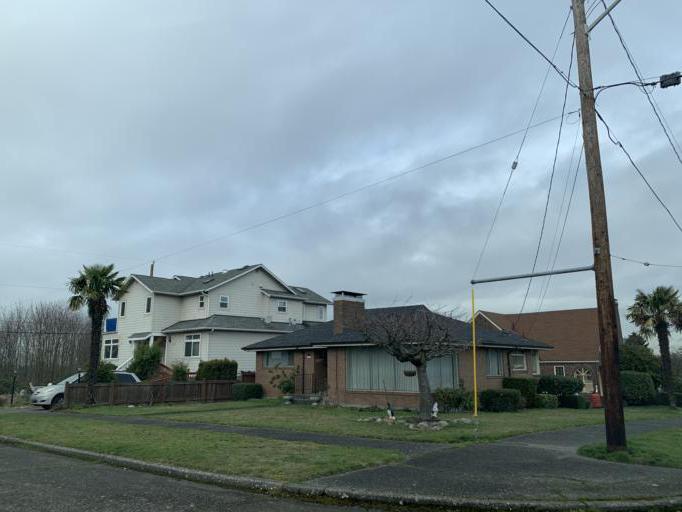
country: US
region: Washington
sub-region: King County
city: Seattle
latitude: 47.5699
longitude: -122.3161
